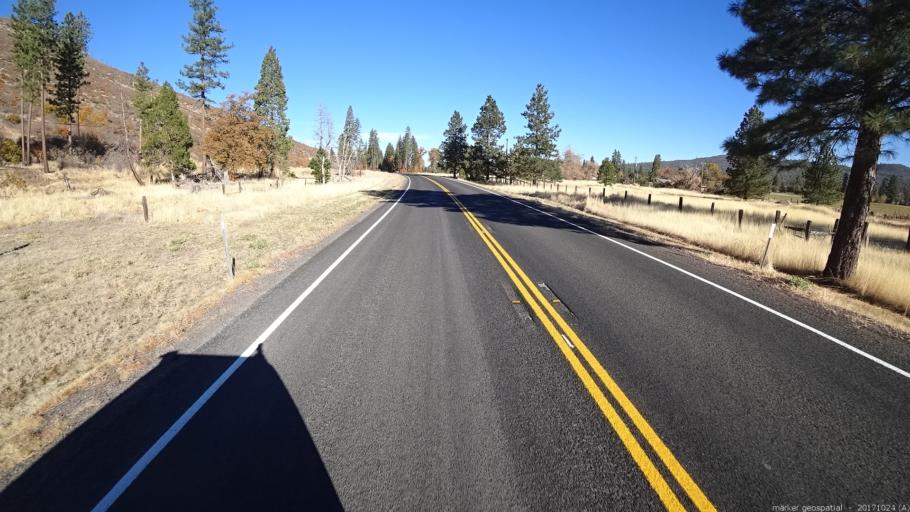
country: US
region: California
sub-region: Shasta County
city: Burney
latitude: 40.8326
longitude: -121.5138
